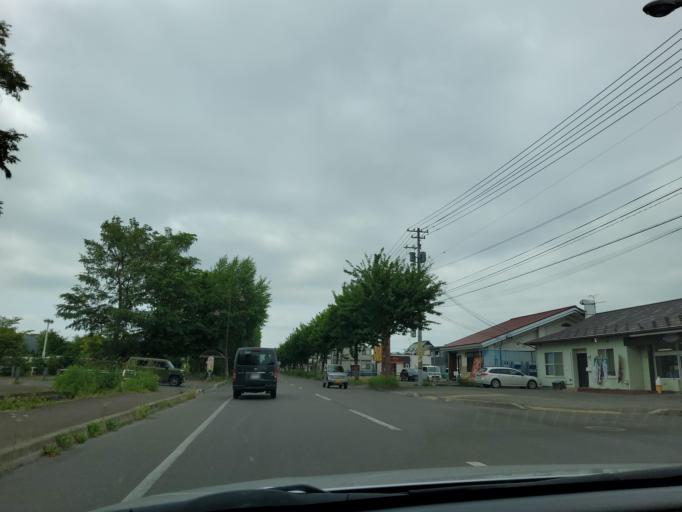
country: JP
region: Hokkaido
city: Obihiro
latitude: 42.9127
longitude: 143.1444
